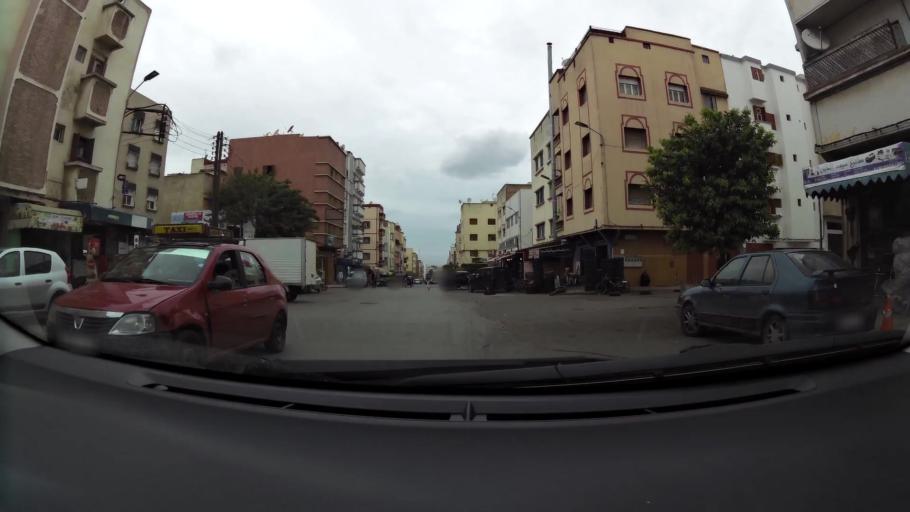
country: MA
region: Grand Casablanca
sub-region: Casablanca
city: Casablanca
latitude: 33.5702
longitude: -7.5507
